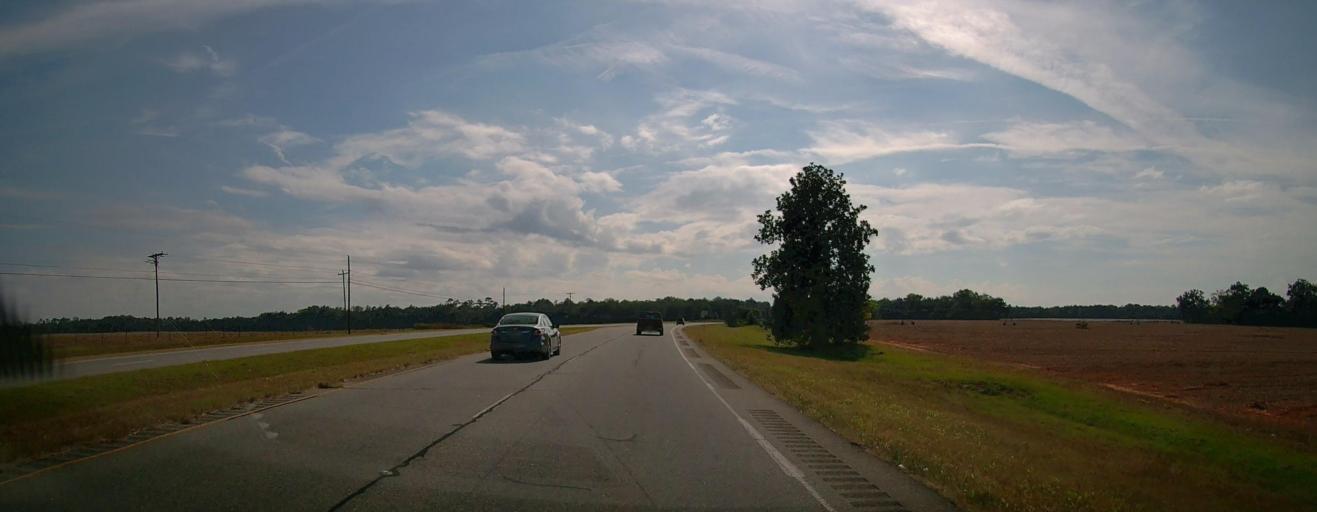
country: US
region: Georgia
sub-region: Dougherty County
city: Putney
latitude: 31.3632
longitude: -84.1549
